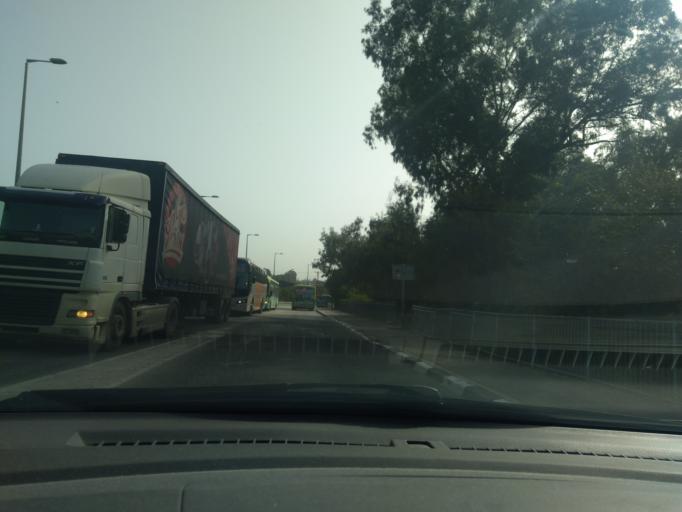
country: IL
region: Central District
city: Netanya
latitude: 32.3245
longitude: 34.8690
